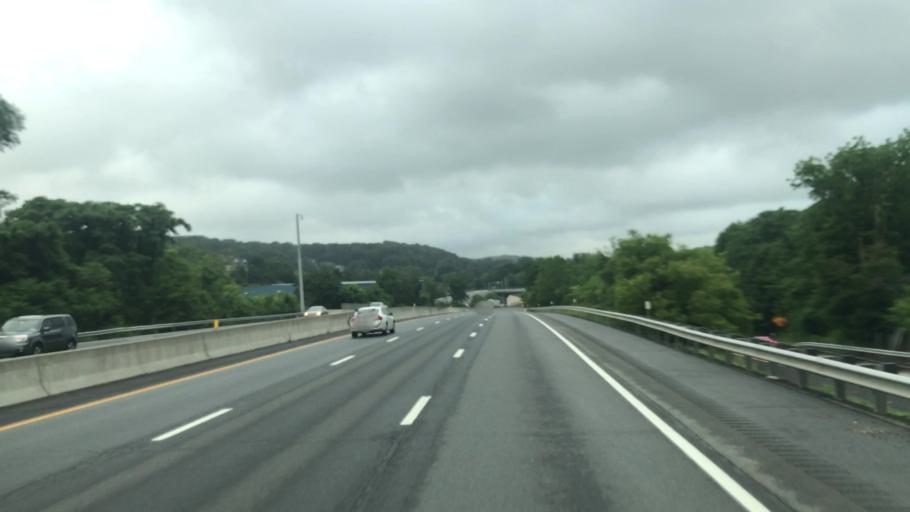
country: US
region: New York
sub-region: Westchester County
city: Ardsley
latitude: 41.0073
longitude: -73.8513
